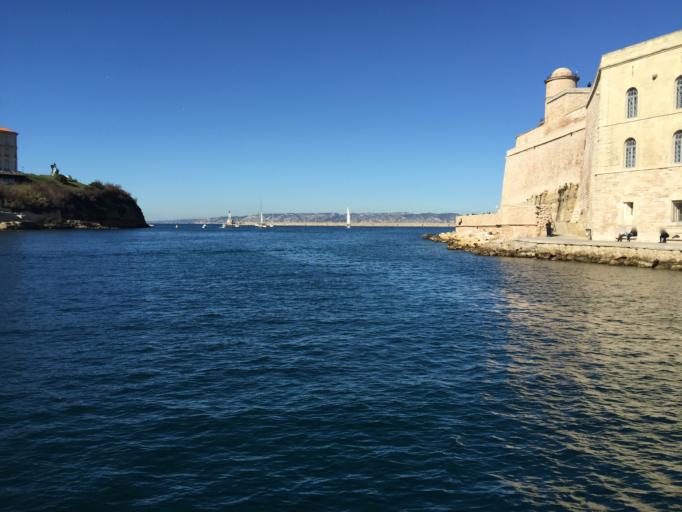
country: FR
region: Provence-Alpes-Cote d'Azur
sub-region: Departement des Bouches-du-Rhone
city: Marseille 02
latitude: 43.2944
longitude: 5.3626
